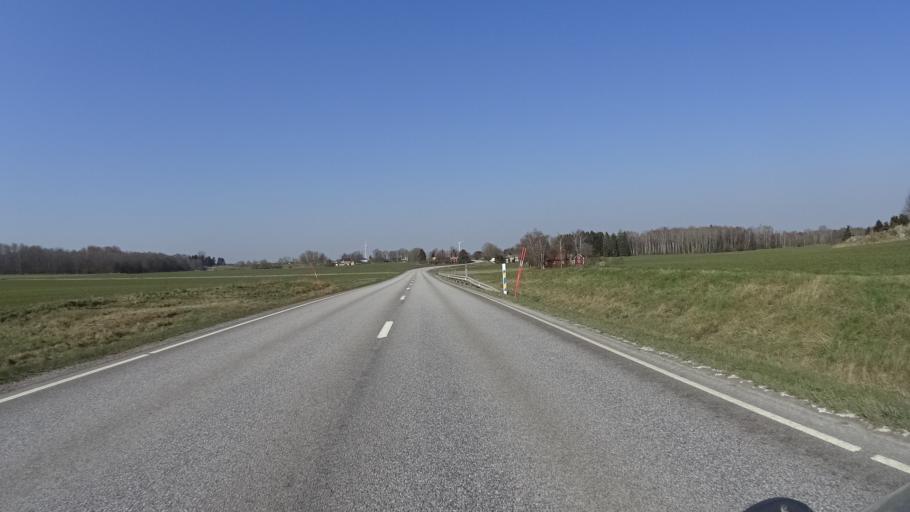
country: SE
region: OEstergoetland
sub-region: Mjolby Kommun
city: Mantorp
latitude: 58.3768
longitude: 15.2665
